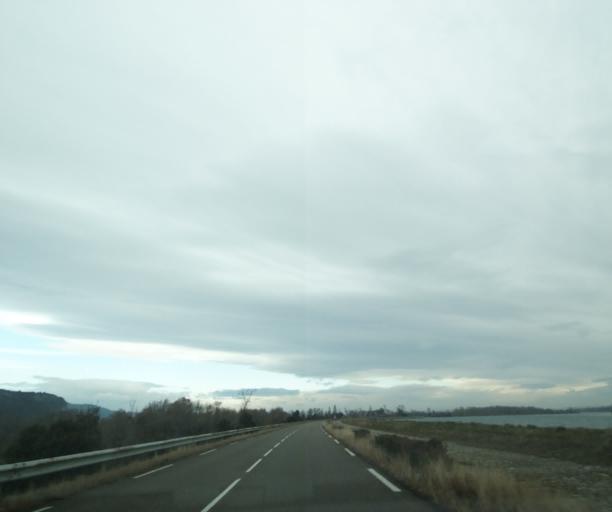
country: FR
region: Rhone-Alpes
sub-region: Departement de l'Ardeche
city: Cornas
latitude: 44.9793
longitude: 4.8561
